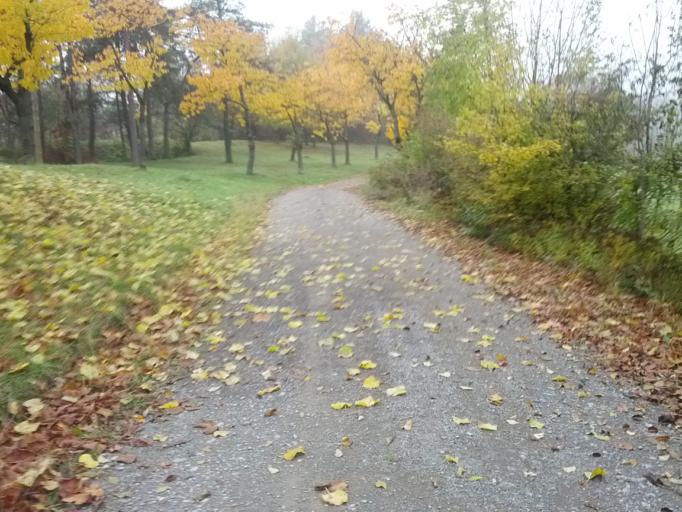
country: DE
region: Thuringia
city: Eisenach
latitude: 50.9698
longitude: 10.3653
